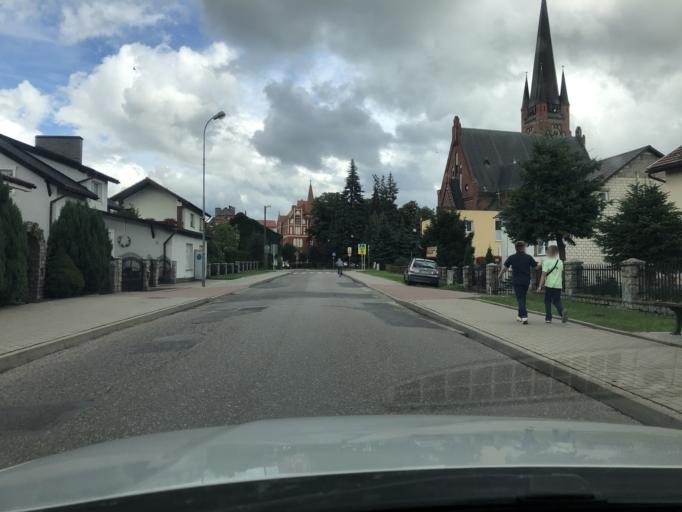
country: PL
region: Lubusz
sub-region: Powiat strzelecko-drezdenecki
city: Drezdenko
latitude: 52.8381
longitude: 15.8266
